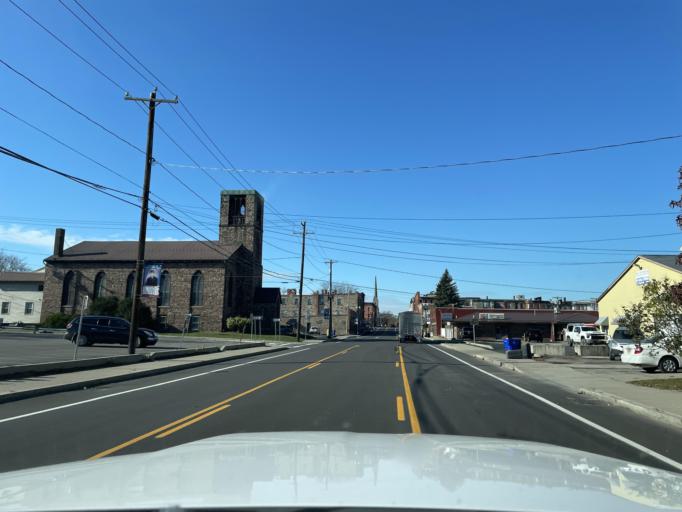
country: US
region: New York
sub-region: Orleans County
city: Medina
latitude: 43.2205
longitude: -78.3839
